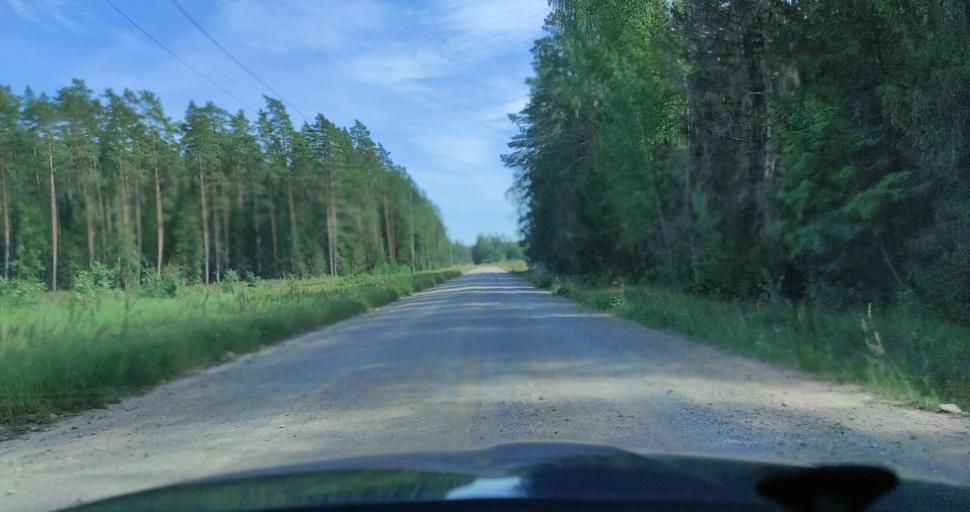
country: LV
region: Durbe
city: Liegi
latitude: 56.7620
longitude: 21.3198
